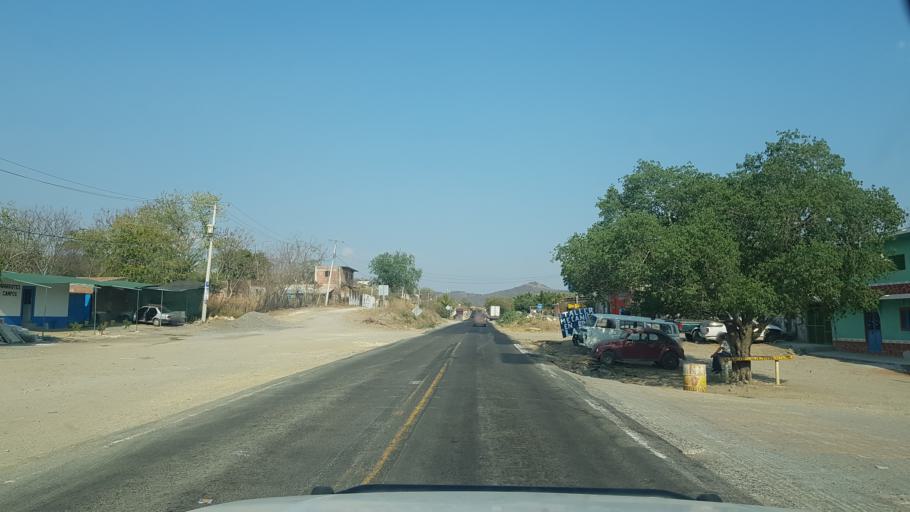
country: MX
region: Puebla
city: Calmeca
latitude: 18.6435
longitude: -98.6306
